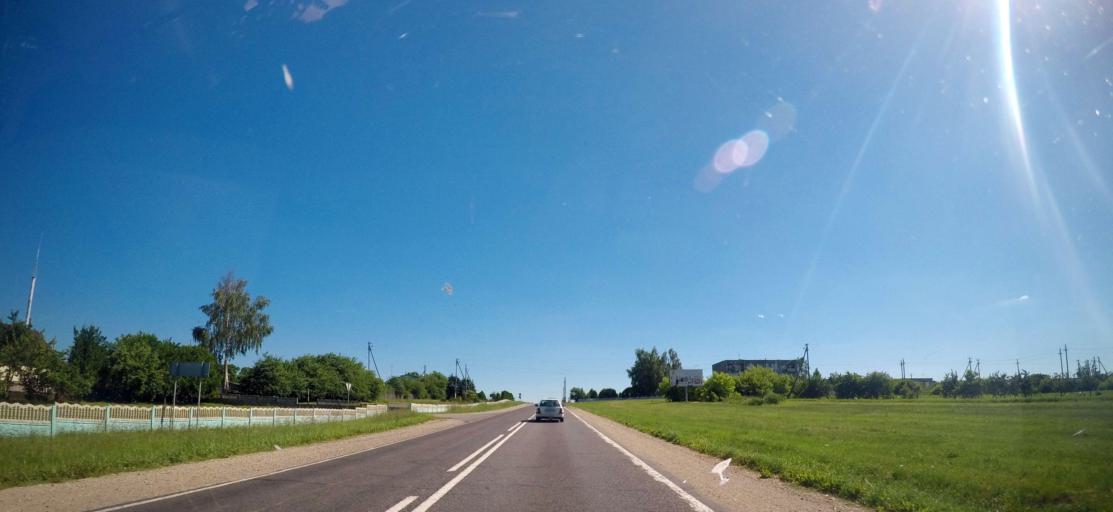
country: BY
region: Grodnenskaya
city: Indura
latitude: 53.4693
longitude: 23.8855
